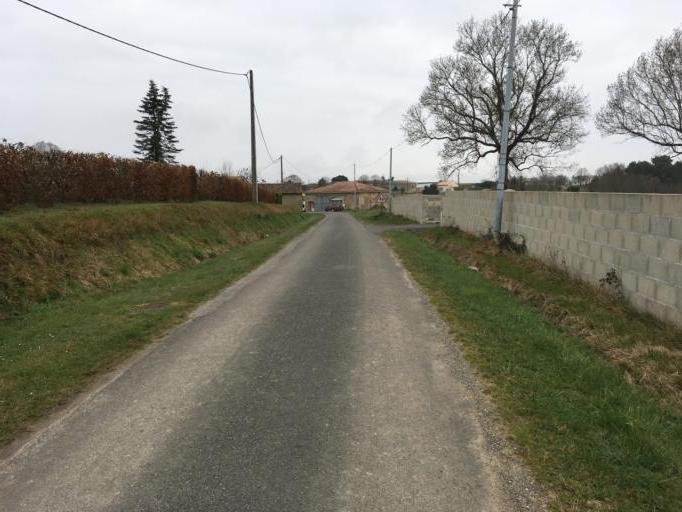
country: FR
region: Poitou-Charentes
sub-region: Departement de la Charente-Maritime
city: Mirambeau
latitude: 45.3429
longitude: -0.5855
